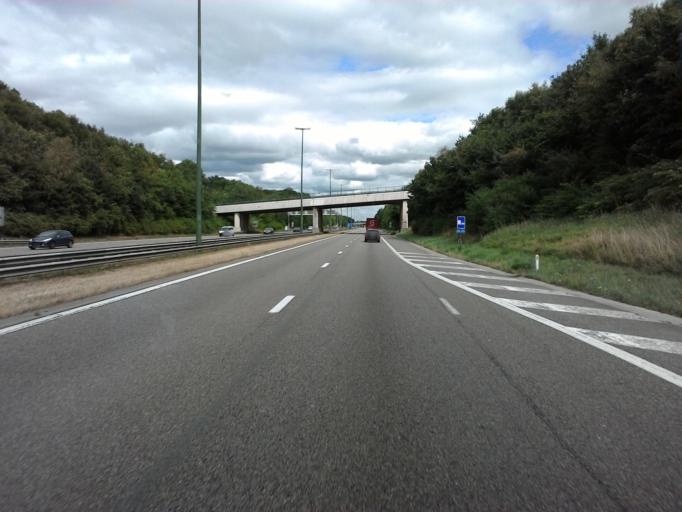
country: BE
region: Wallonia
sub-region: Province du Luxembourg
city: Arlon
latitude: 49.6704
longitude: 5.7850
